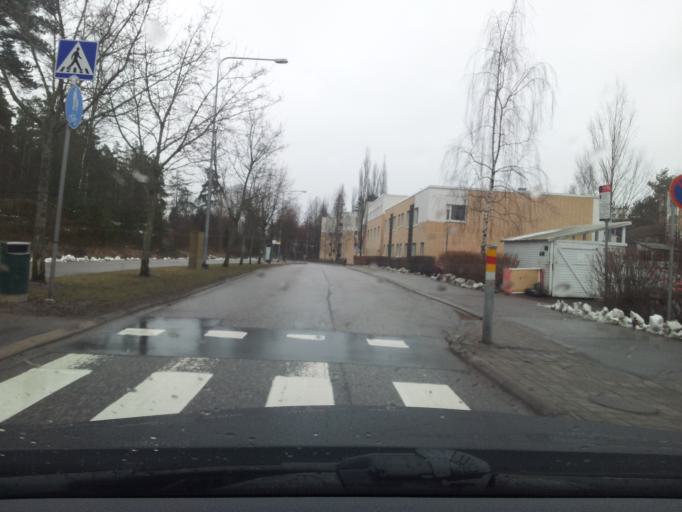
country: FI
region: Uusimaa
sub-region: Helsinki
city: Espoo
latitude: 60.1682
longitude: 24.6780
